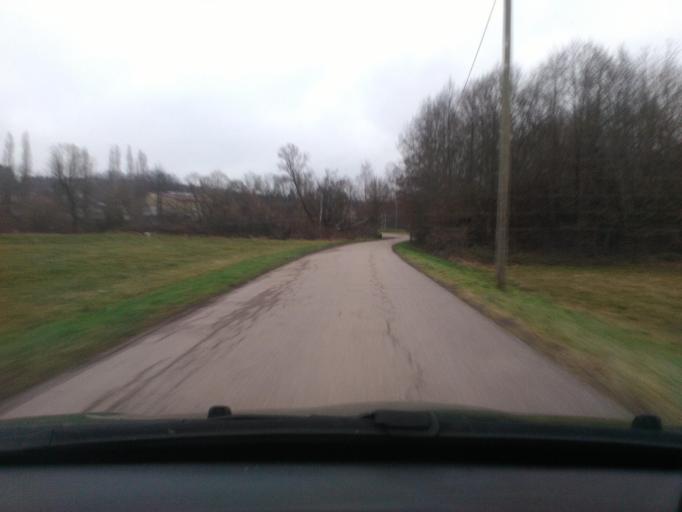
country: FR
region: Lorraine
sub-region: Departement des Vosges
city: Etival-Clairefontaine
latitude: 48.3571
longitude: 6.8737
